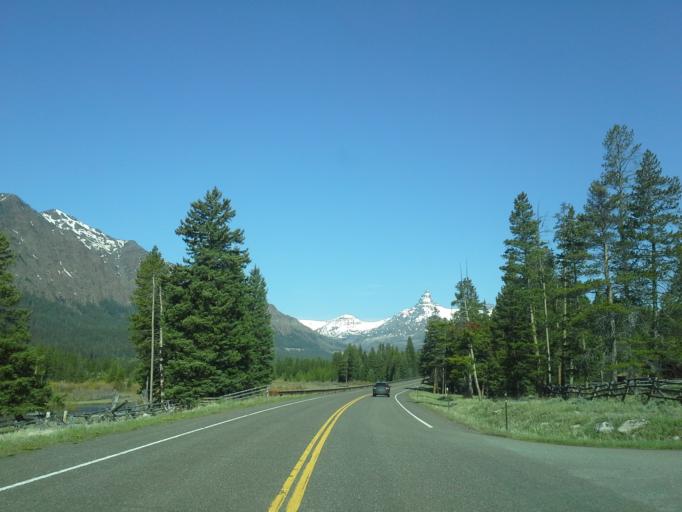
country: US
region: Montana
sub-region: Carbon County
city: Red Lodge
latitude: 44.9365
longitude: -109.7625
